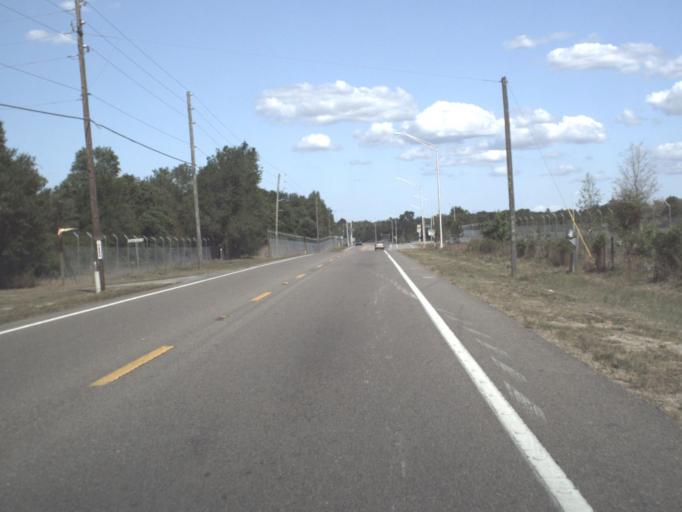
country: US
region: Florida
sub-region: Lake County
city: Mount Plymouth
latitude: 28.8127
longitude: -81.5089
